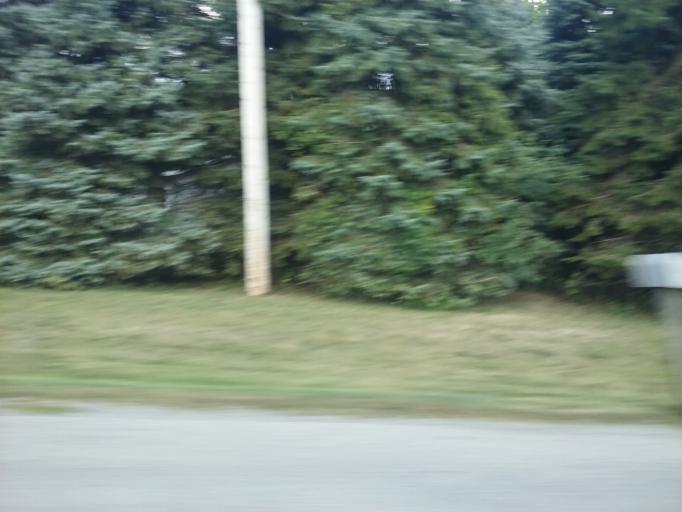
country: US
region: Ohio
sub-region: Wood County
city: Bowling Green
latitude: 41.3010
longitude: -83.6503
